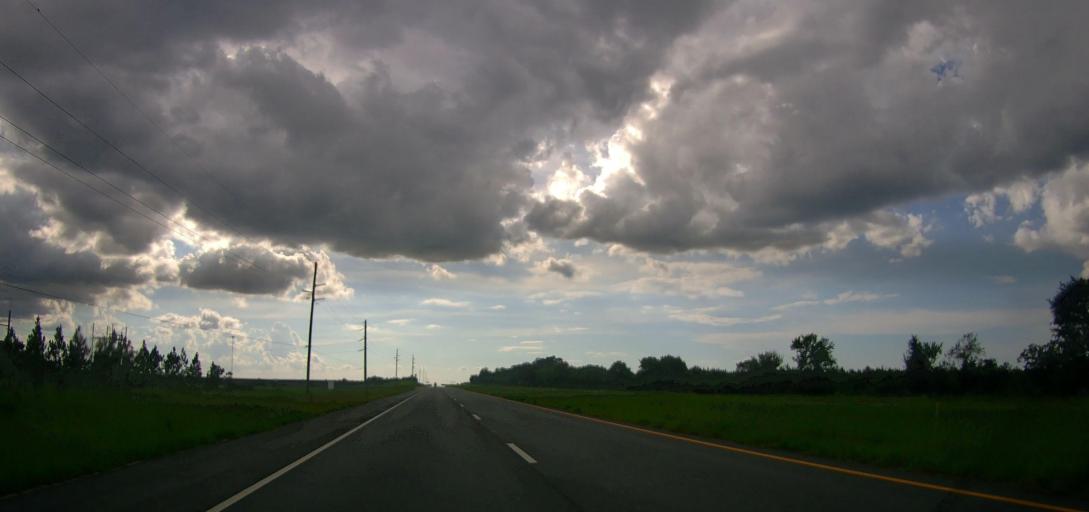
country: US
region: Georgia
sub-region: Taylor County
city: Butler
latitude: 32.5772
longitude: -84.3105
